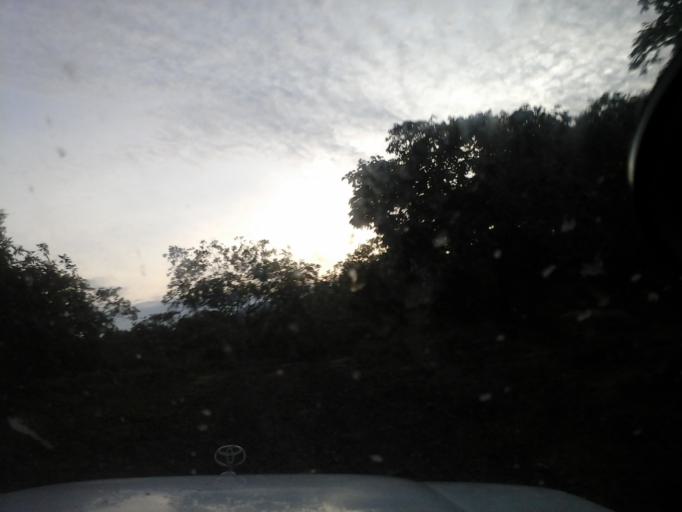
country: CO
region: Cesar
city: Agustin Codazzi
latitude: 10.1713
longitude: -73.1687
